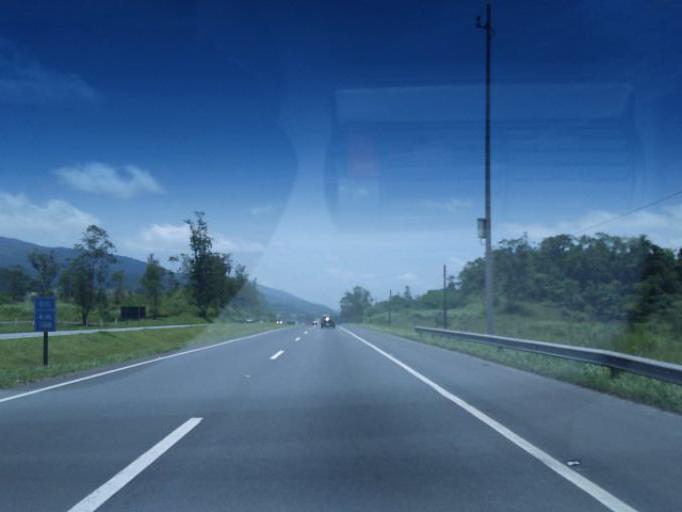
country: BR
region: Sao Paulo
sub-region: Miracatu
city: Miracatu
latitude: -24.2692
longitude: -47.3981
